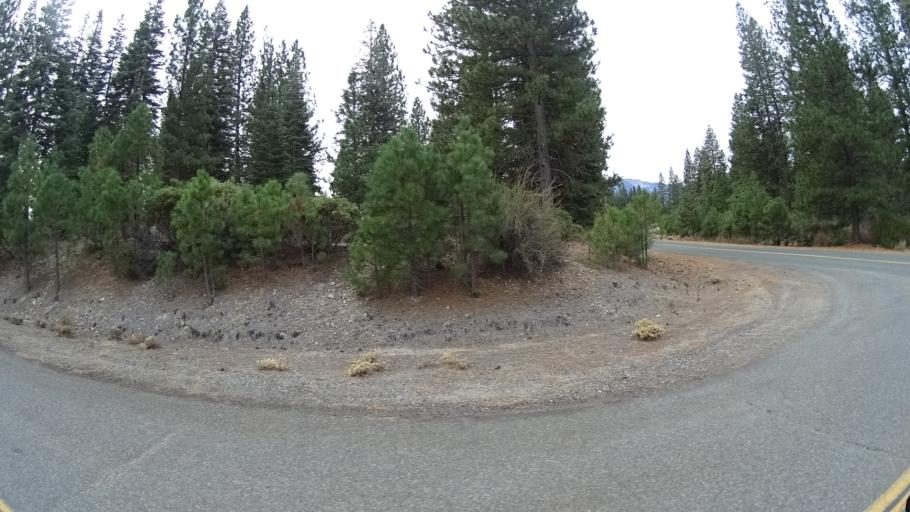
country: US
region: California
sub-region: Siskiyou County
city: Weed
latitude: 41.4107
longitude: -122.3716
